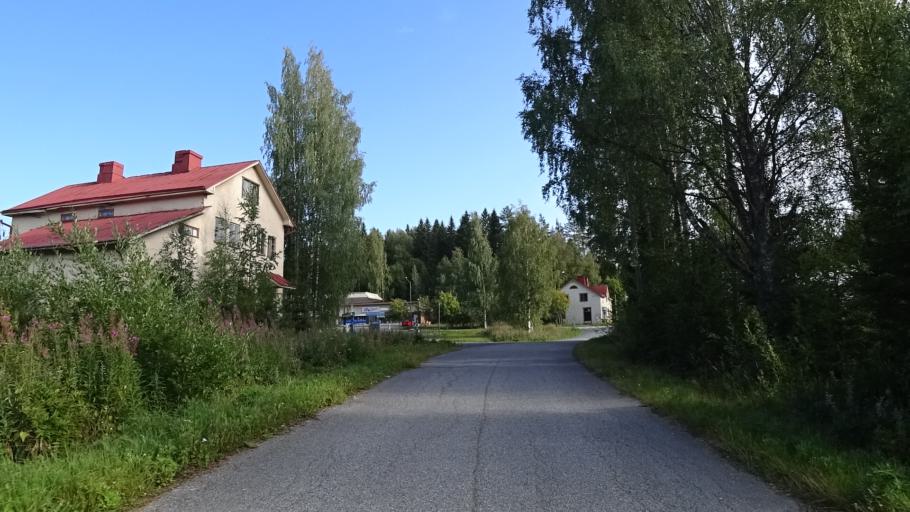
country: FI
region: North Karelia
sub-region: Joensuu
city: Eno
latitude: 62.7992
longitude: 30.1504
